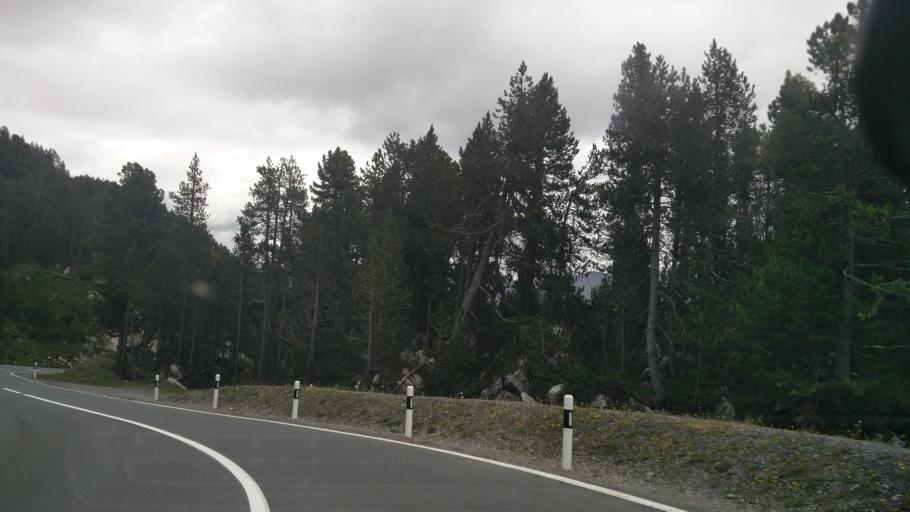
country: IT
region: Lombardy
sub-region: Provincia di Sondrio
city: Isolaccia
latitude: 46.6387
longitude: 10.2986
